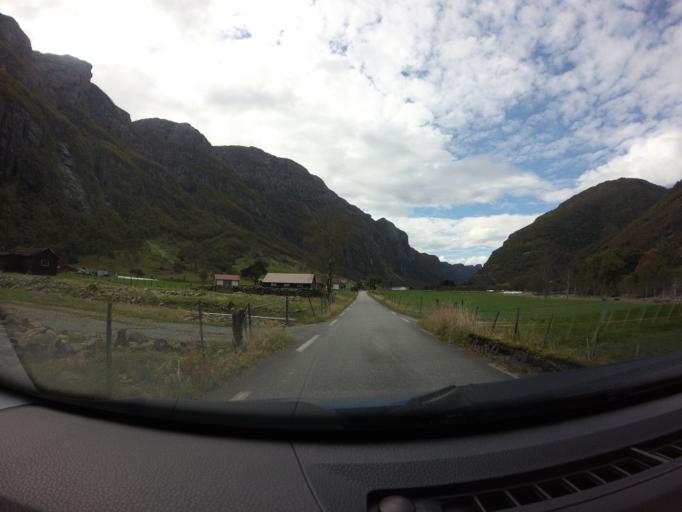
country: NO
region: Rogaland
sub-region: Forsand
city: Forsand
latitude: 58.8457
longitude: 6.3636
